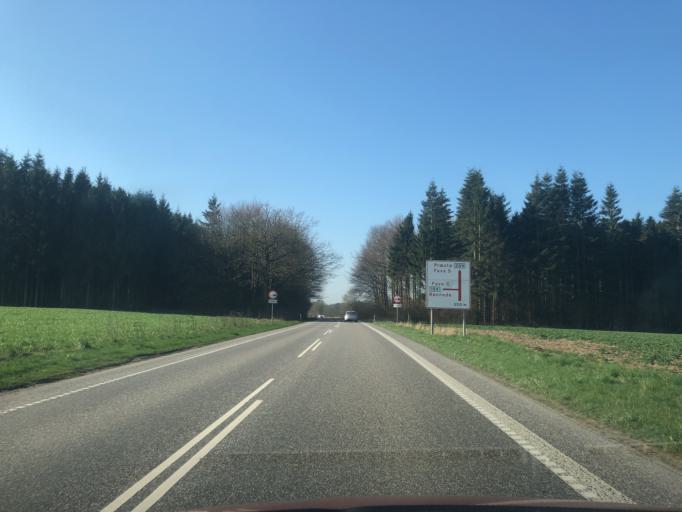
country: DK
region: Zealand
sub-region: Faxe Kommune
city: Fakse
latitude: 55.2610
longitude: 12.0985
